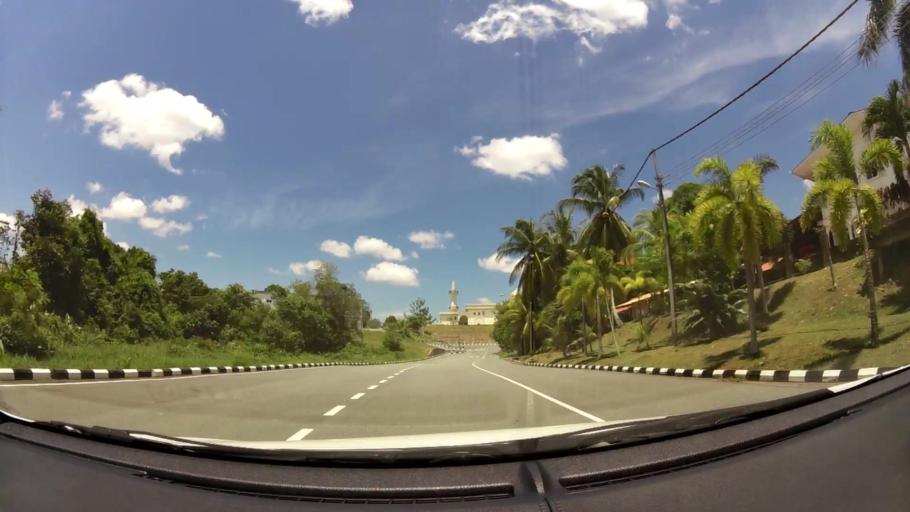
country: BN
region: Brunei and Muara
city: Bandar Seri Begawan
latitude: 4.9362
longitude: 114.9655
